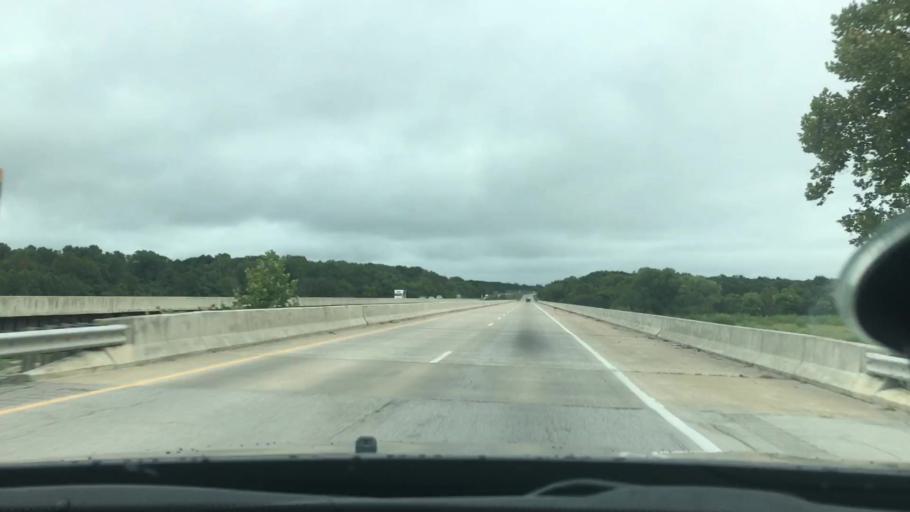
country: US
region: Oklahoma
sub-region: Okfuskee County
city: Okemah
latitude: 35.3934
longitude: -96.4024
